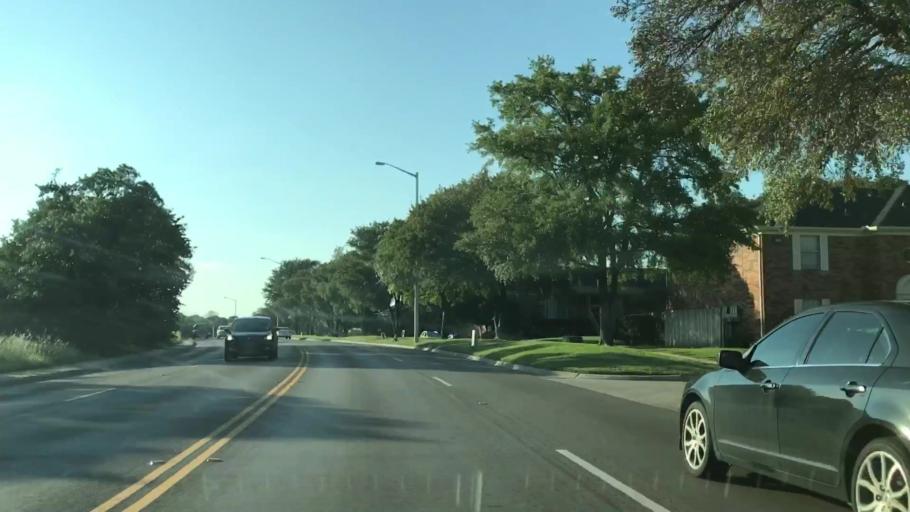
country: US
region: Texas
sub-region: Denton County
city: Denton
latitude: 33.1958
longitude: -97.1082
